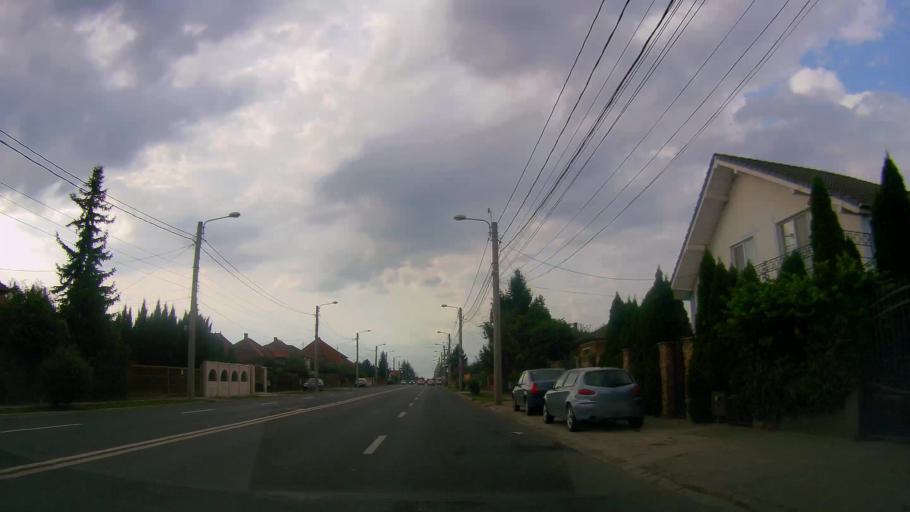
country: RO
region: Satu Mare
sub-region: Municipiul Satu Mare
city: Satu Mare
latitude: 47.7669
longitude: 22.8835
